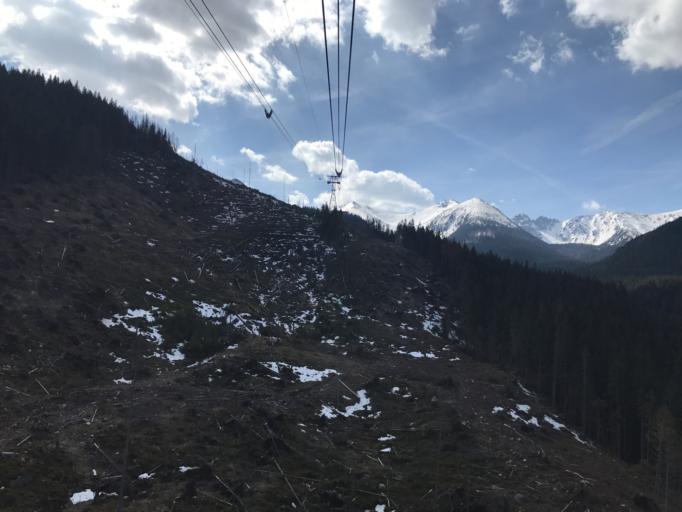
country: PL
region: Lesser Poland Voivodeship
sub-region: Powiat tatrzanski
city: Zakopane
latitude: 49.2640
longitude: 19.9775
